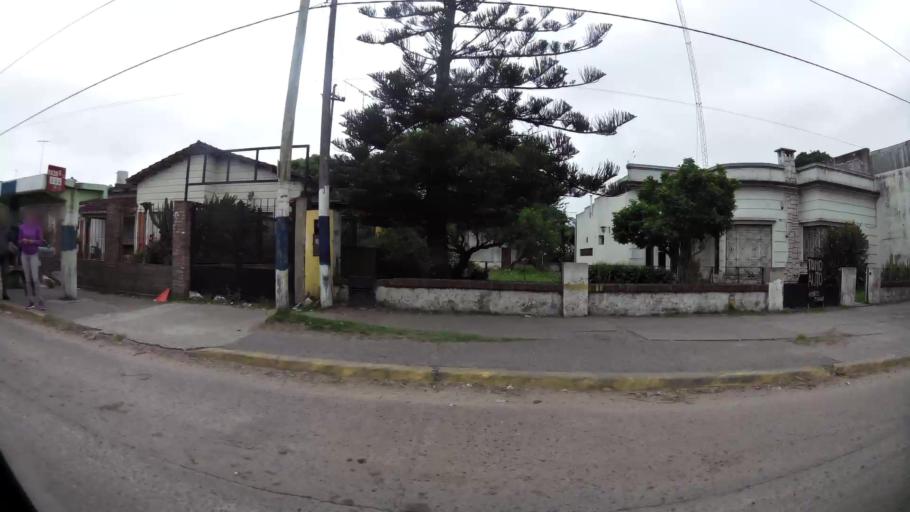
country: AR
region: Buenos Aires
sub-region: Partido de La Plata
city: La Plata
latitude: -34.9614
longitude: -58.0108
